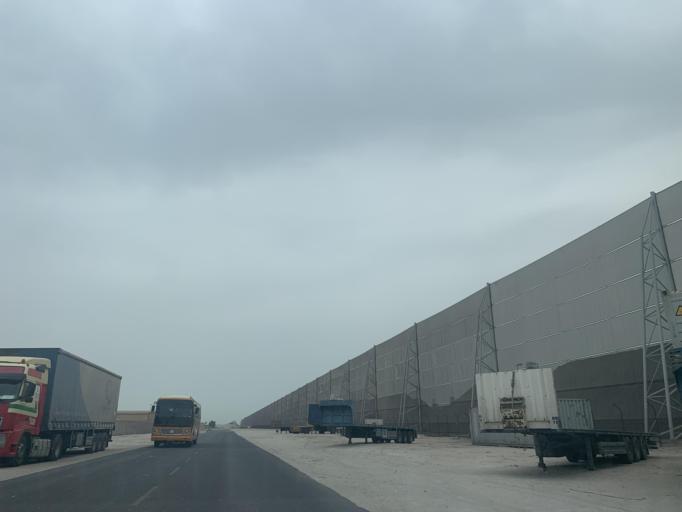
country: BH
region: Muharraq
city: Al Hadd
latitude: 26.2070
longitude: 50.6800
